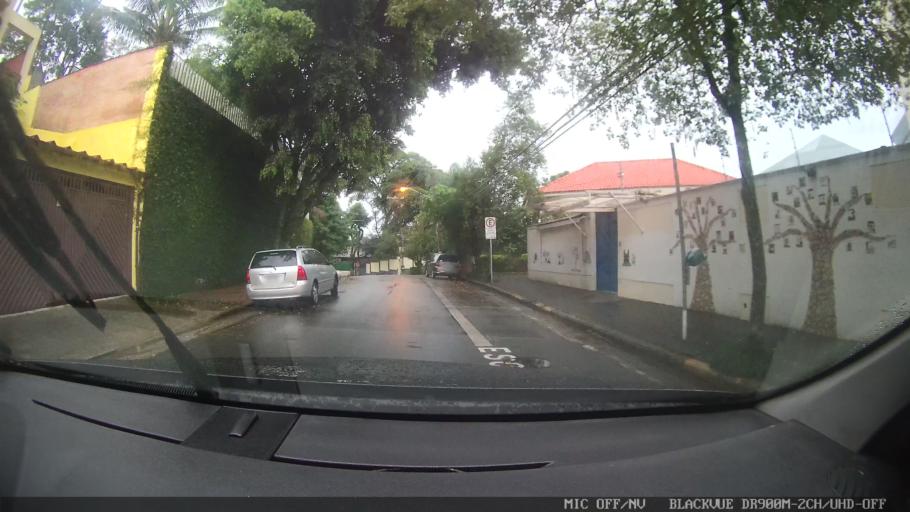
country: BR
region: Sao Paulo
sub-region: Sao Paulo
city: Sao Paulo
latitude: -23.5481
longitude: -46.6802
